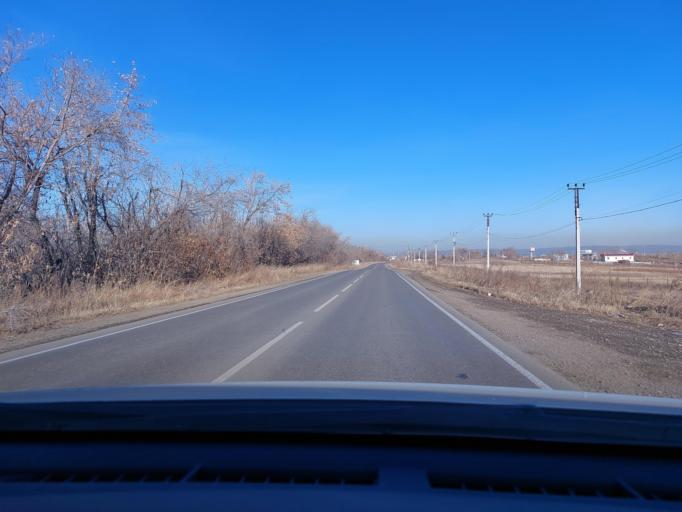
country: RU
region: Irkutsk
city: Smolenshchina
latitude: 52.3209
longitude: 104.1824
